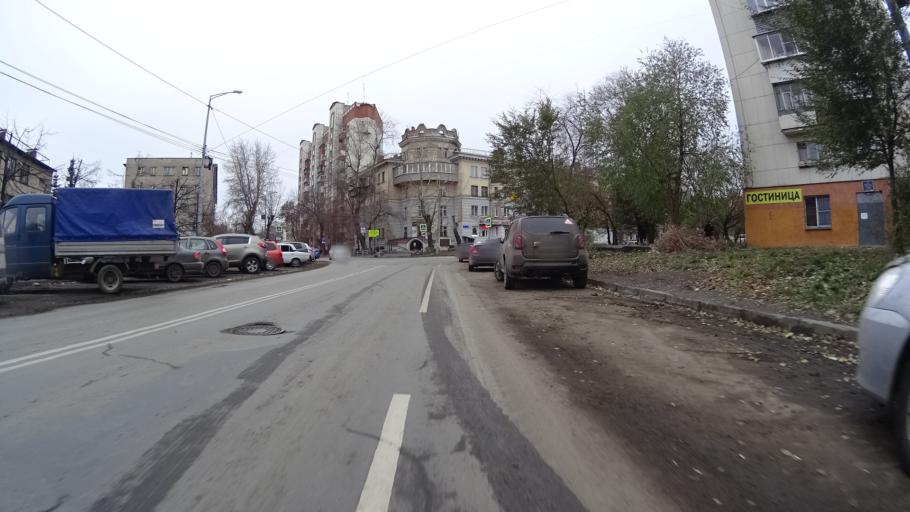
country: RU
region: Chelyabinsk
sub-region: Gorod Chelyabinsk
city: Chelyabinsk
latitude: 55.1511
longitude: 61.4177
